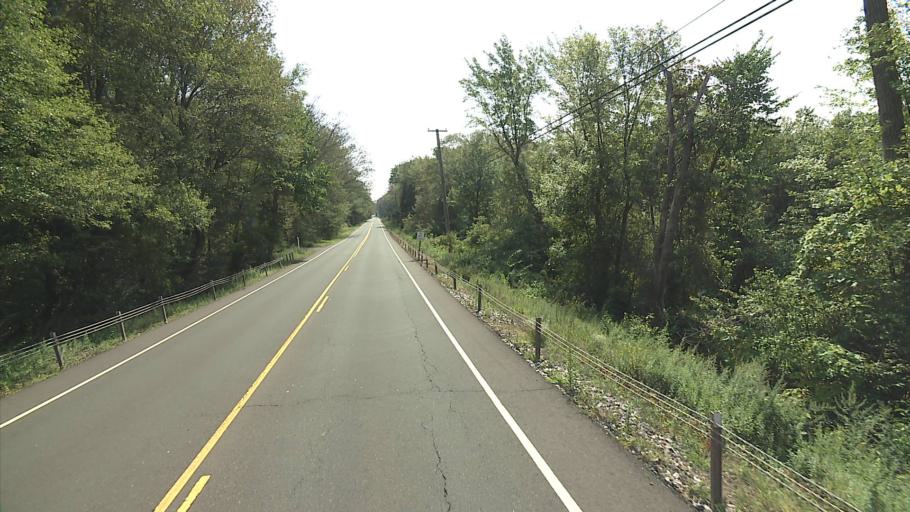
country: US
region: Connecticut
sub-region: Middlesex County
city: Durham
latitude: 41.4420
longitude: -72.6590
